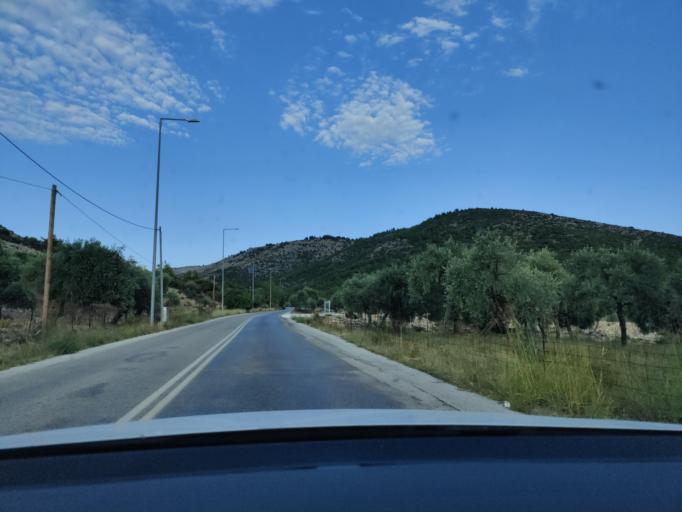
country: GR
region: East Macedonia and Thrace
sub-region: Nomos Kavalas
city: Limenaria
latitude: 40.6135
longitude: 24.6249
